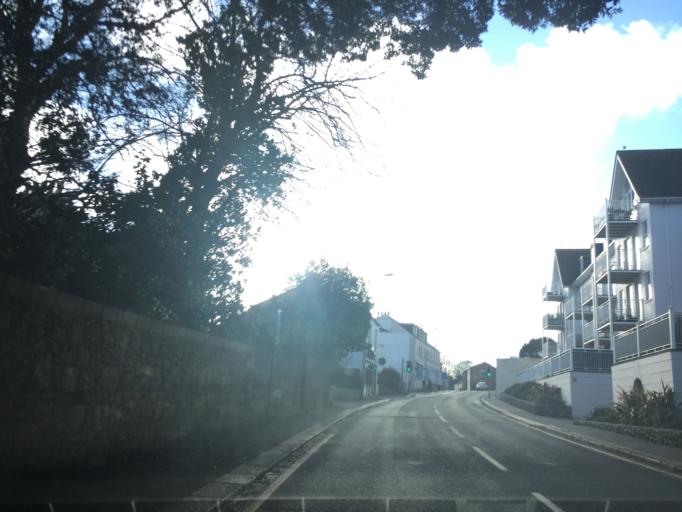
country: JE
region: St Helier
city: Saint Helier
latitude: 49.1984
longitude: -2.1367
